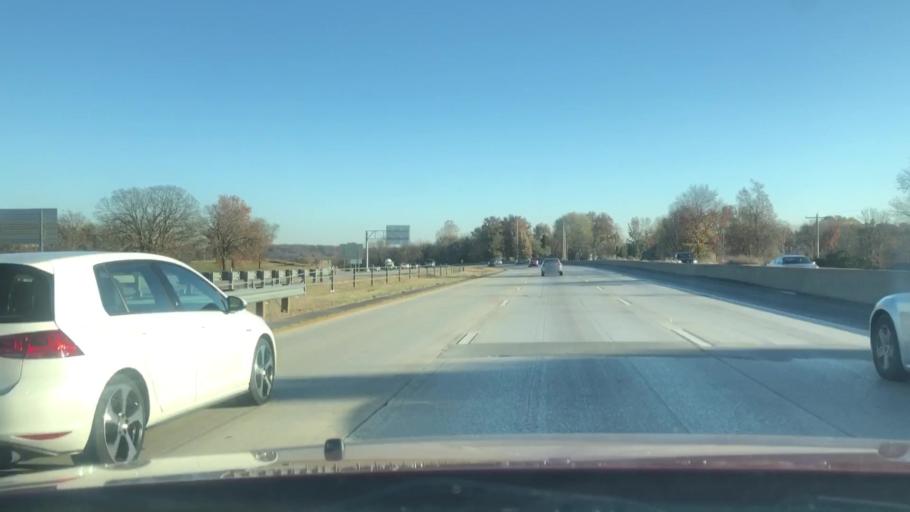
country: US
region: Missouri
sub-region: Greene County
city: Springfield
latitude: 37.1340
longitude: -93.2459
